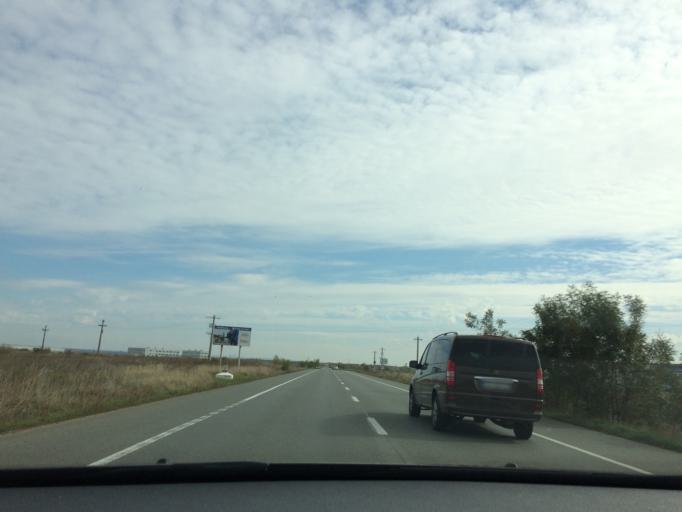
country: RO
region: Timis
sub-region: Comuna Ghiroda
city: Giarmata-Vii
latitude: 45.8139
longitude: 21.2717
